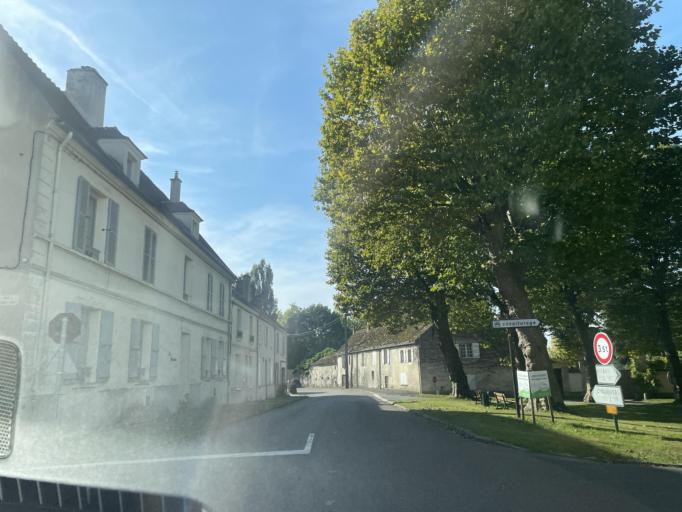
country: FR
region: Ile-de-France
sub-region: Departement de Seine-et-Marne
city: Saint-Jean-les-Deux-Jumeaux
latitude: 48.9413
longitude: 2.9858
